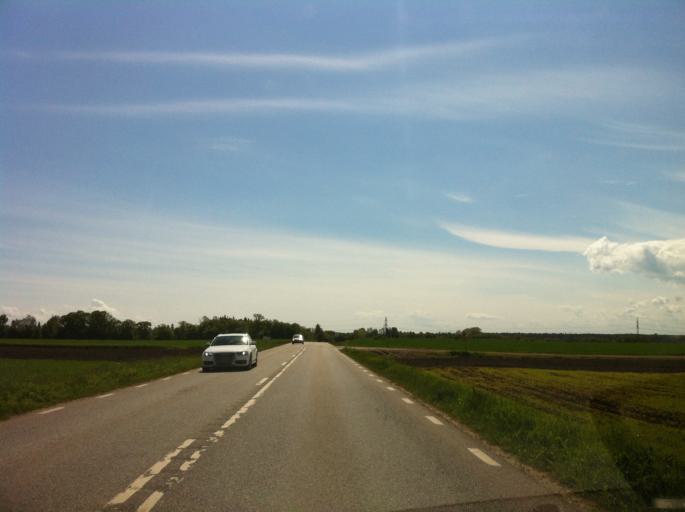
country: SE
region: Skane
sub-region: Landskrona
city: Asmundtorp
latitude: 55.8556
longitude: 12.9723
